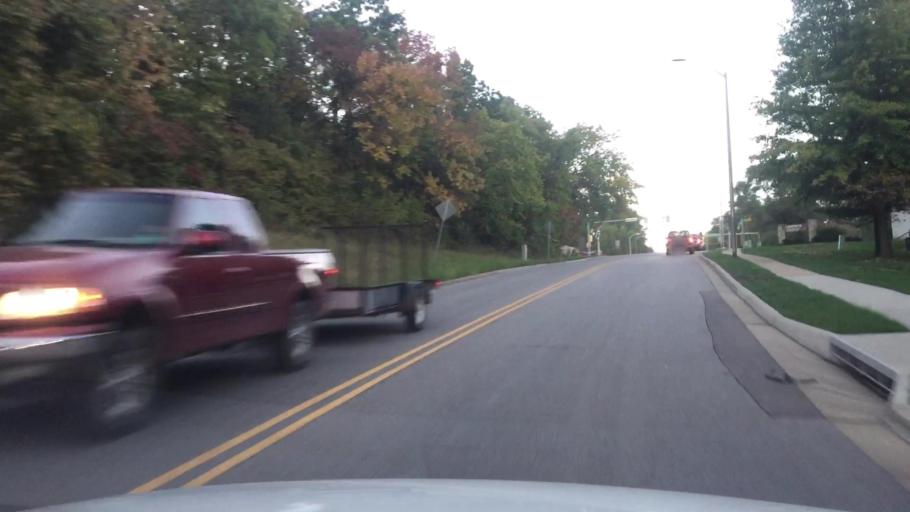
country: US
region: Kansas
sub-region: Johnson County
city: Shawnee
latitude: 39.0235
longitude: -94.7426
